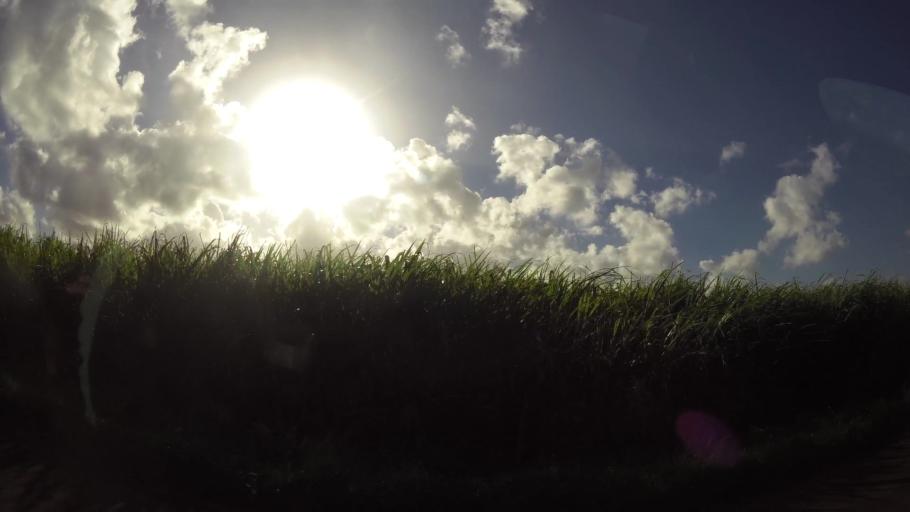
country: MQ
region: Martinique
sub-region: Martinique
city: Ducos
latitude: 14.5987
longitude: -60.9759
